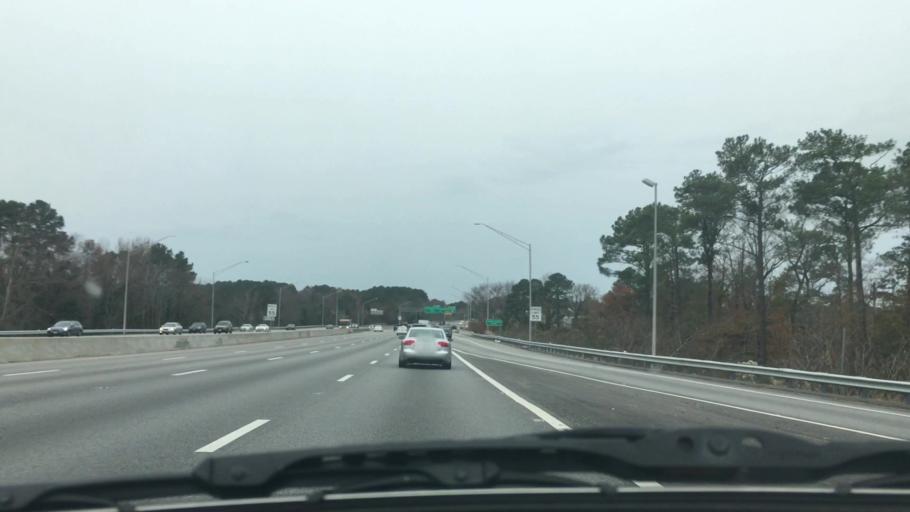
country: US
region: Virginia
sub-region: City of Virginia Beach
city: Virginia Beach
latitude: 36.8379
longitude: -76.0575
